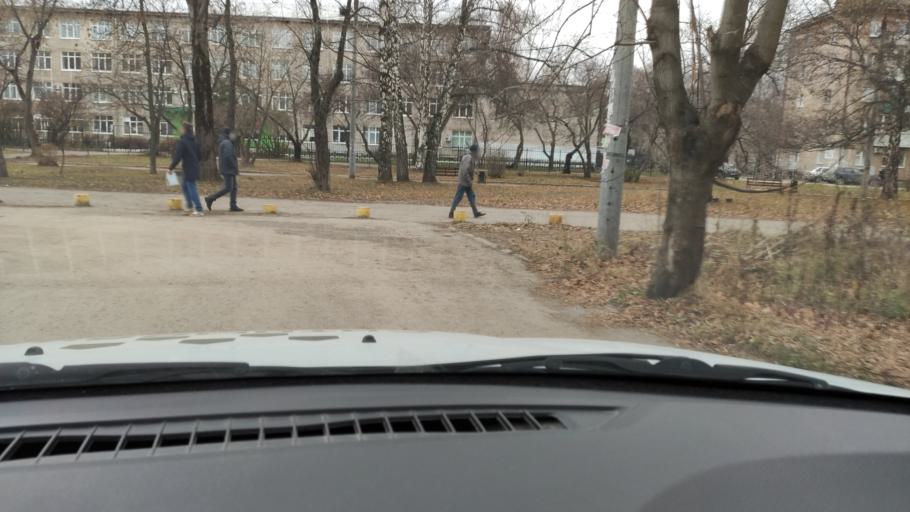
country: RU
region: Perm
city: Perm
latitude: 58.0099
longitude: 56.2862
